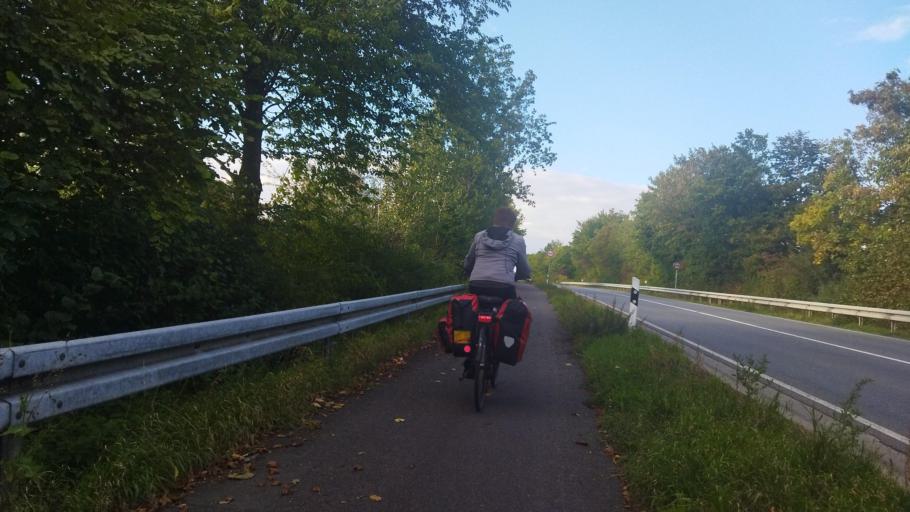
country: DE
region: North Rhine-Westphalia
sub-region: Regierungsbezirk Munster
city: Billerbeck
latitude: 51.9379
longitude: 7.2616
